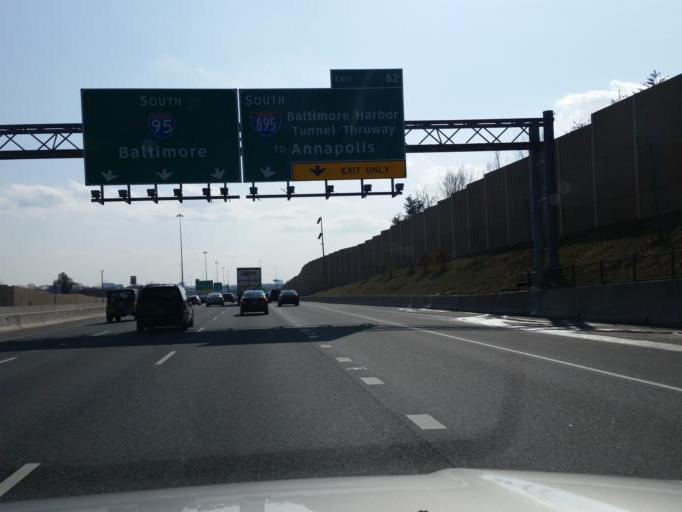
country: US
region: Maryland
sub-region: Baltimore County
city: Rosedale
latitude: 39.3288
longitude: -76.5241
